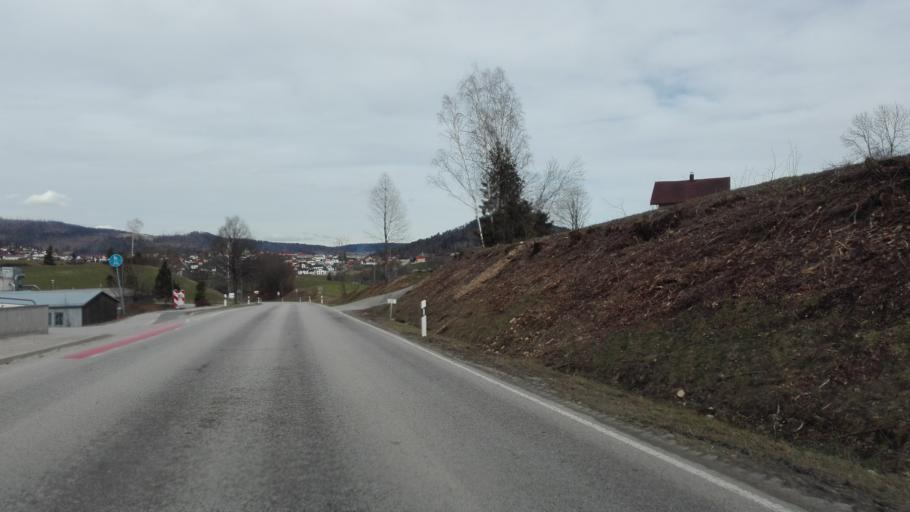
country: DE
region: Bavaria
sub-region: Lower Bavaria
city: Hauzenberg
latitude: 48.6438
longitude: 13.6042
